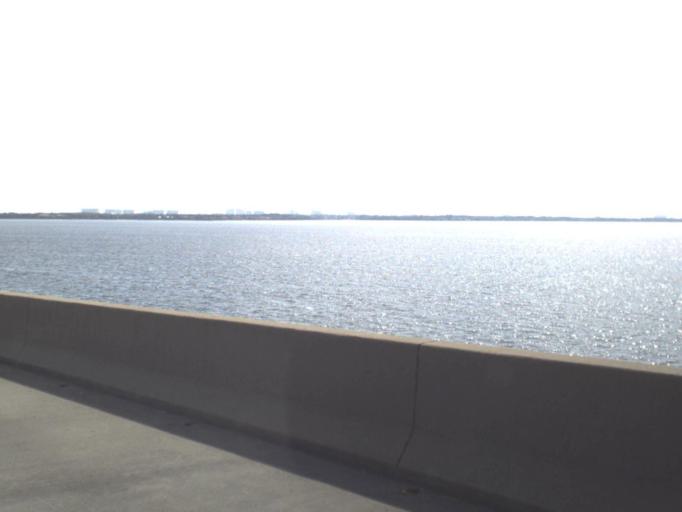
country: US
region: Florida
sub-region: Walton County
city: Miramar Beach
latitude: 30.4289
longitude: -86.4190
